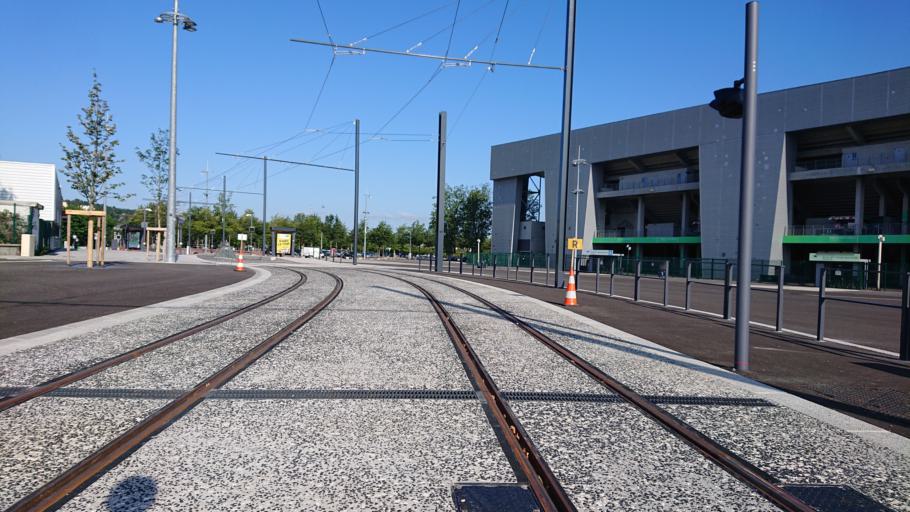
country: FR
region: Rhone-Alpes
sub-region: Departement de la Loire
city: Saint-Priest-en-Jarez
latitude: 45.4590
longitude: 4.3903
